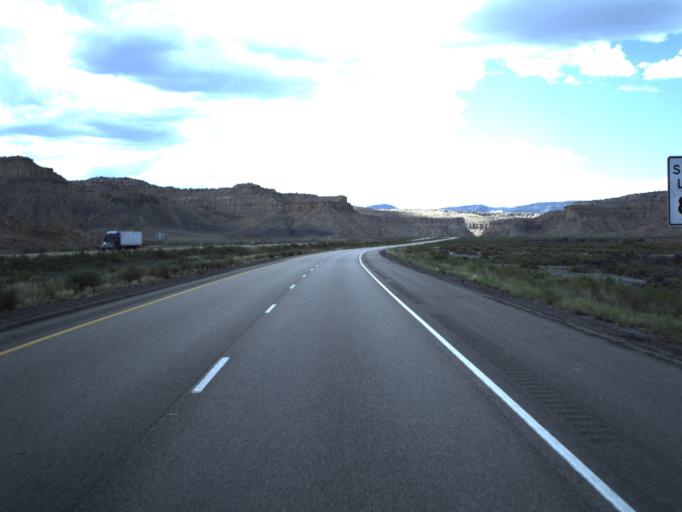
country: US
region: Utah
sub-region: Emery County
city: Ferron
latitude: 38.8101
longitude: -111.2255
